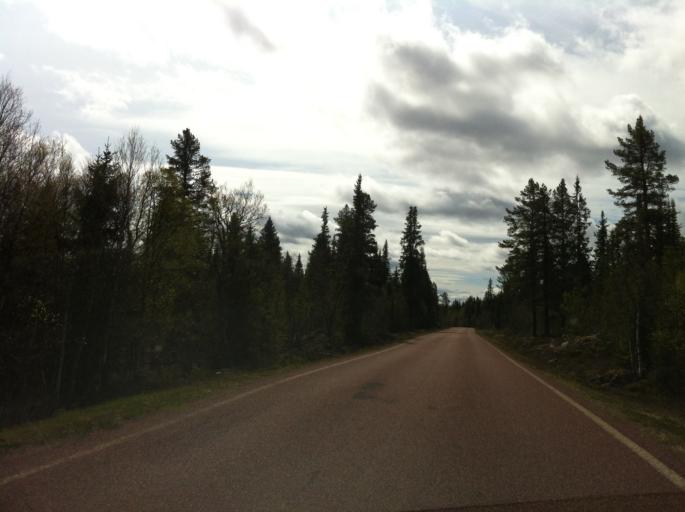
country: NO
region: Hedmark
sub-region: Engerdal
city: Engerdal
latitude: 62.1605
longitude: 12.9441
